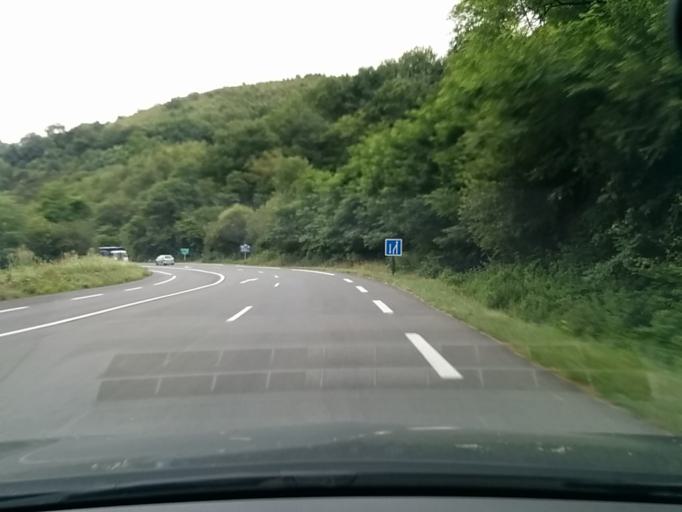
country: FR
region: Aquitaine
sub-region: Departement des Pyrenees-Atlantiques
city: Saint-Jean-Pied-de-Port
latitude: 43.1861
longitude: -1.2565
